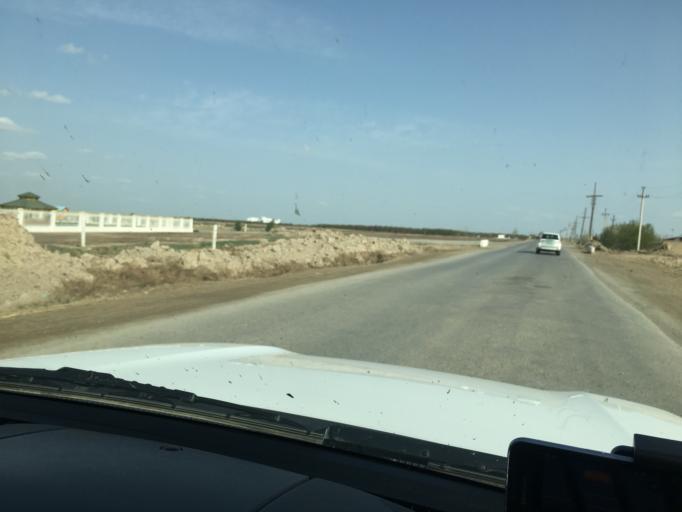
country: TM
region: Lebap
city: Farap
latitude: 39.2293
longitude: 63.5176
